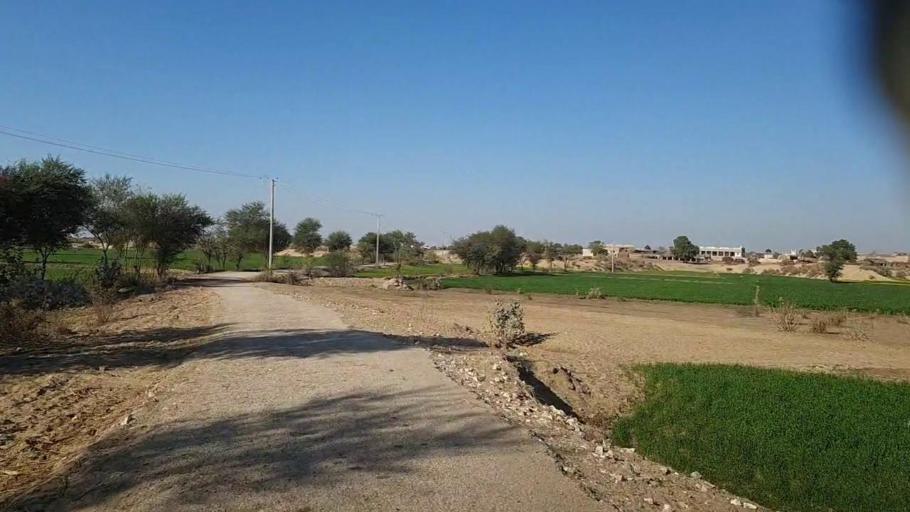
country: PK
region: Sindh
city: Khairpur
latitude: 27.9197
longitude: 69.7513
